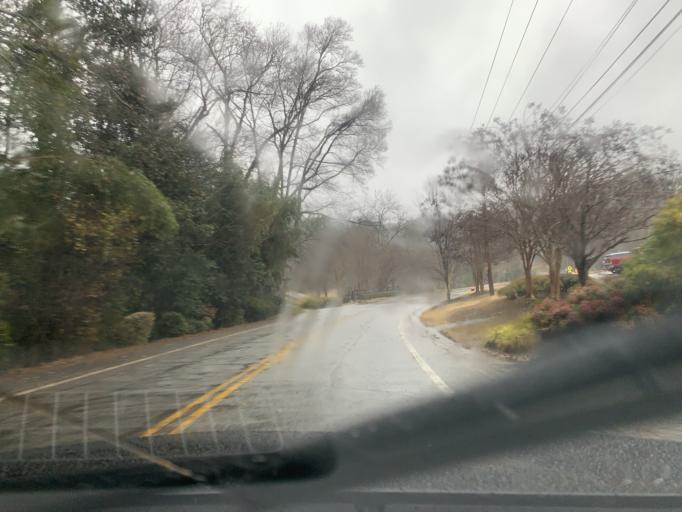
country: US
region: South Carolina
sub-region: Greenville County
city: Greenville
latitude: 34.8408
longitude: -82.3871
